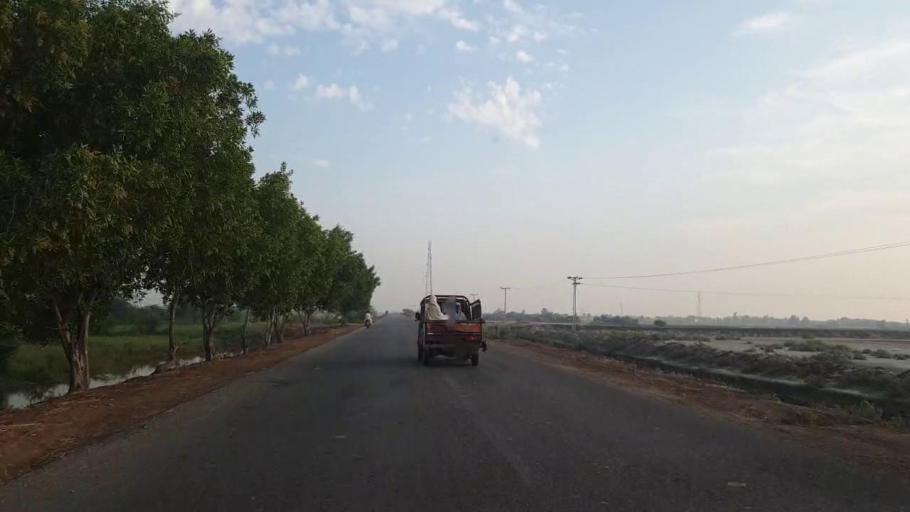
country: PK
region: Sindh
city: Badin
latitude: 24.6949
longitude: 68.9192
